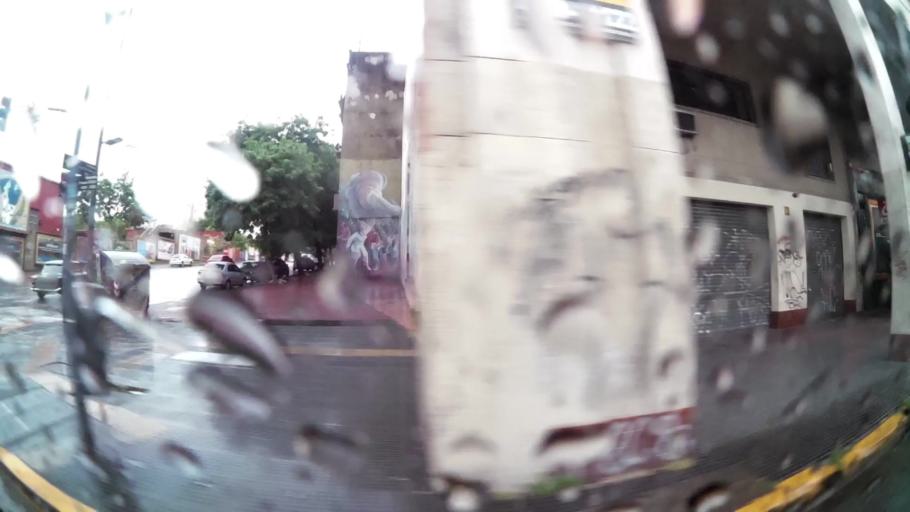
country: AR
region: Buenos Aires F.D.
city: Buenos Aires
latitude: -34.6239
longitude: -58.3681
